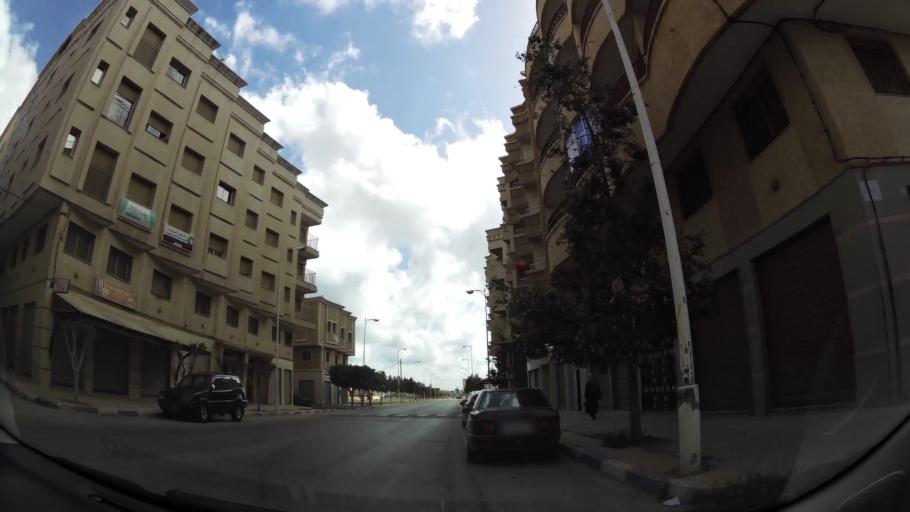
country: MA
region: Oriental
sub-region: Nador
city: Nador
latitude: 35.1633
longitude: -2.9219
